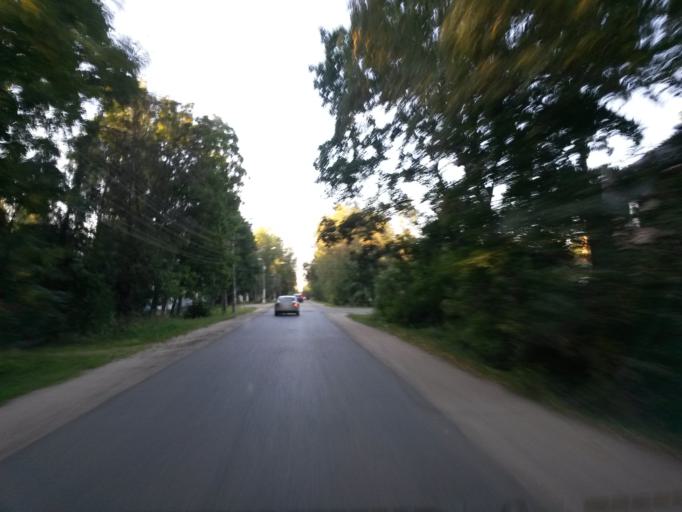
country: RU
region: Moskovskaya
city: Mamontovka
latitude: 55.9782
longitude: 37.8369
